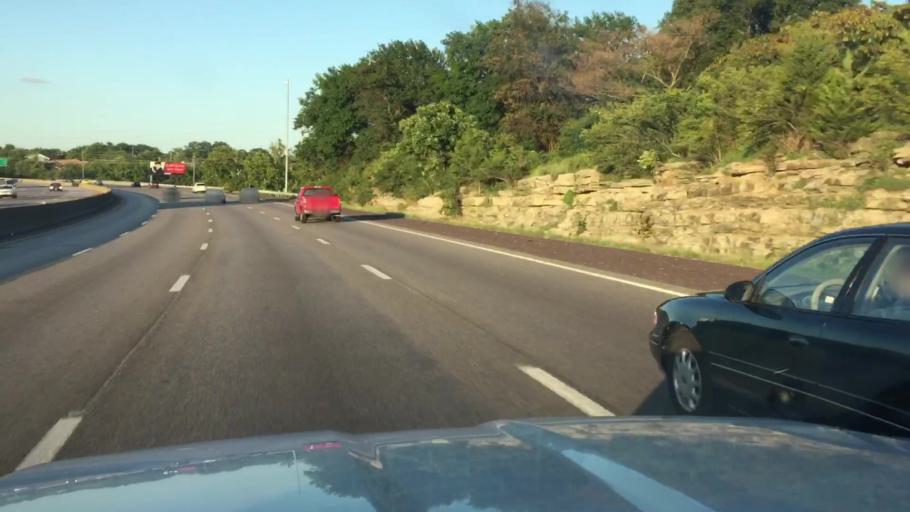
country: US
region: Missouri
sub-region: Saint Louis County
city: Mehlville
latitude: 38.5218
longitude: -90.3234
